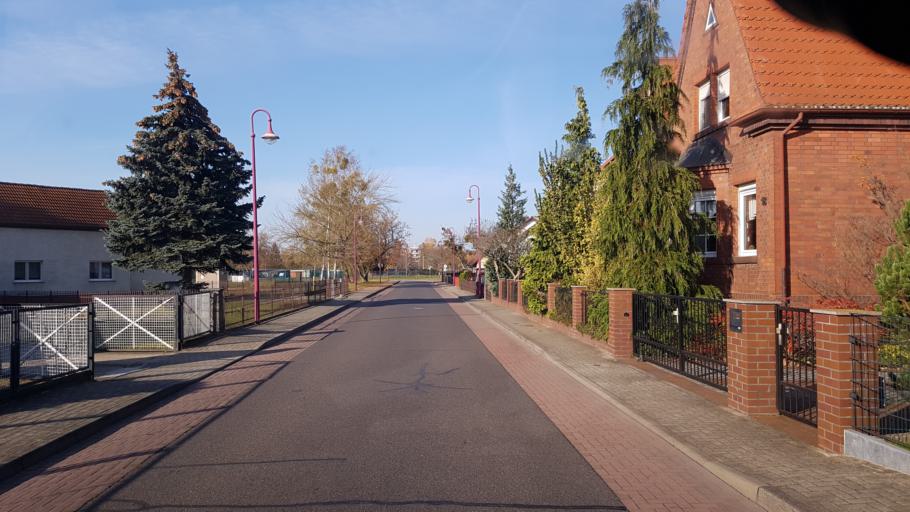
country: DE
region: Brandenburg
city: Grossraschen
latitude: 51.5906
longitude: 14.0075
